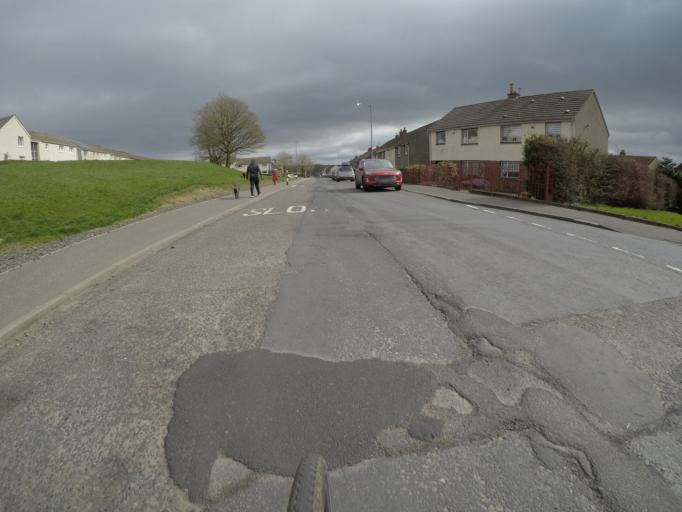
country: GB
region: Scotland
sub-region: East Ayrshire
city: Stewarton
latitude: 55.6791
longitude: -4.5264
